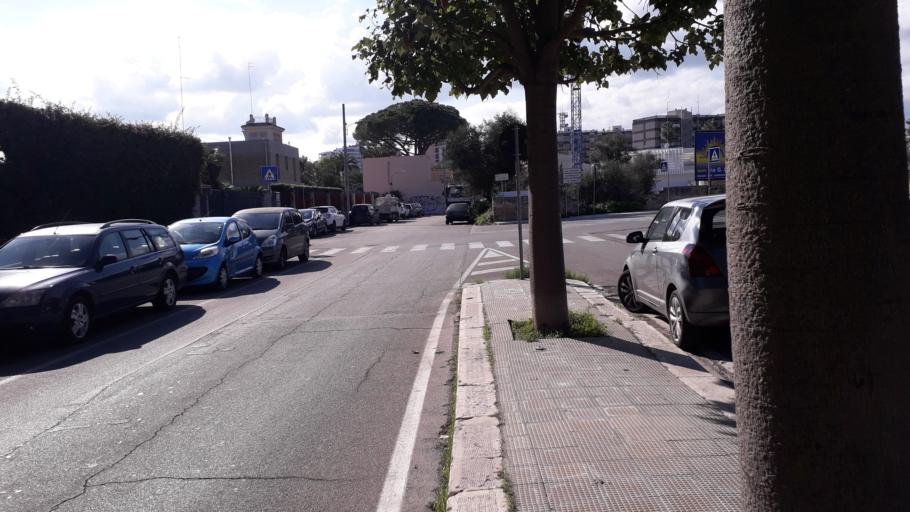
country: IT
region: Apulia
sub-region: Provincia di Bari
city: Bari
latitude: 41.1120
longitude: 16.8552
